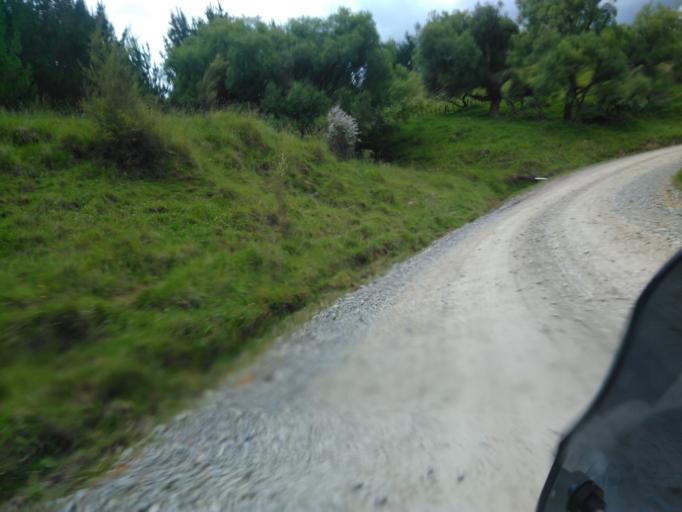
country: NZ
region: Gisborne
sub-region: Gisborne District
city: Gisborne
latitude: -38.0906
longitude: 178.0816
